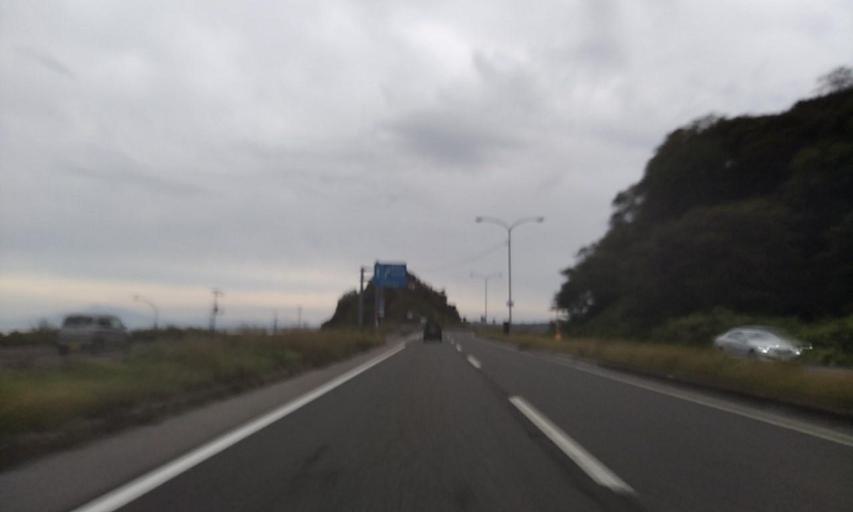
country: JP
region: Hokkaido
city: Abashiri
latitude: 43.9930
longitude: 144.2969
